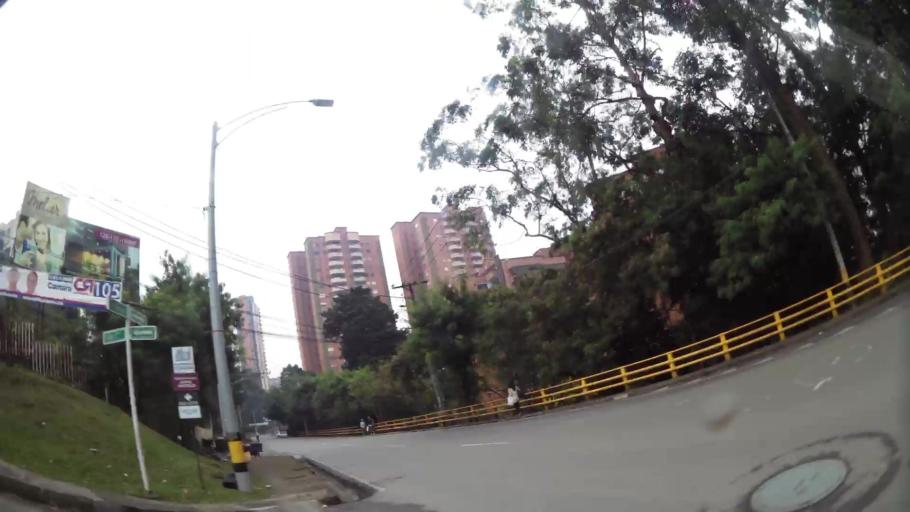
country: CO
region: Antioquia
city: Envigado
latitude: 6.1959
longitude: -75.5659
